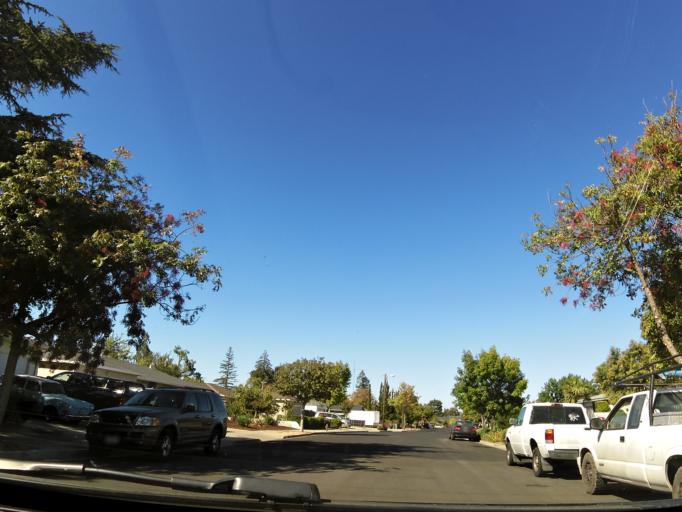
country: US
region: California
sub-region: Santa Clara County
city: Campbell
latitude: 37.2692
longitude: -121.9711
